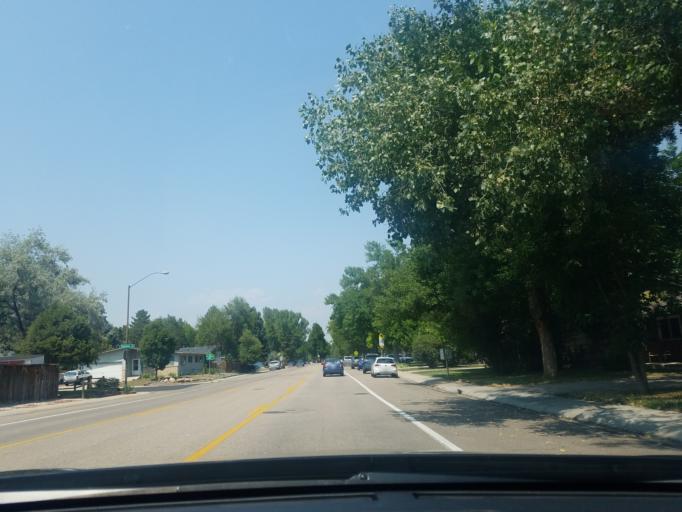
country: US
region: Colorado
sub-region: Larimer County
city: Fort Collins
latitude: 40.5541
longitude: -105.0675
